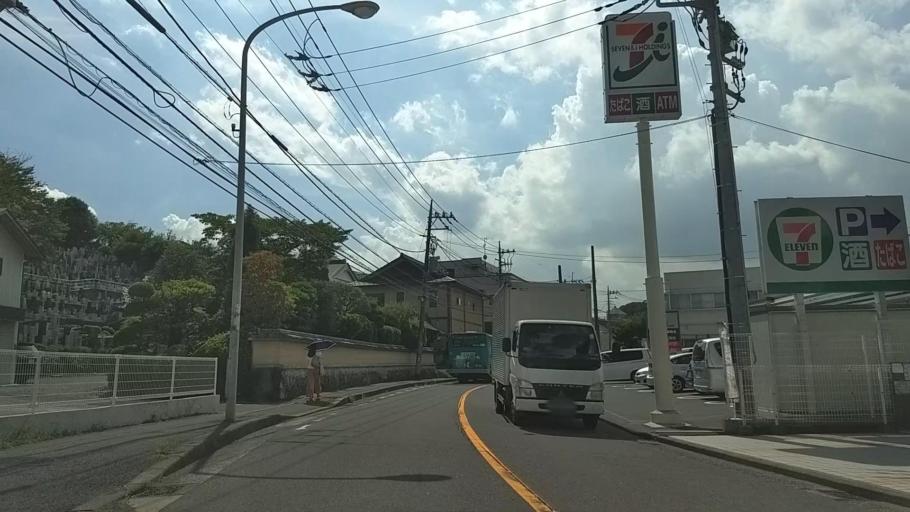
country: JP
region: Kanagawa
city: Yokohama
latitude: 35.5106
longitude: 139.5718
